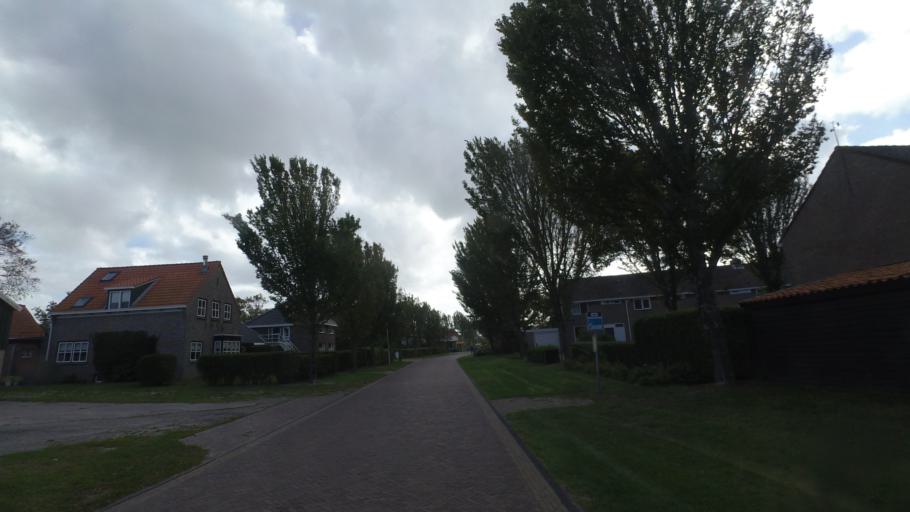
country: NL
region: Friesland
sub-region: Gemeente Ameland
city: Hollum
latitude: 53.4436
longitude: 5.6400
